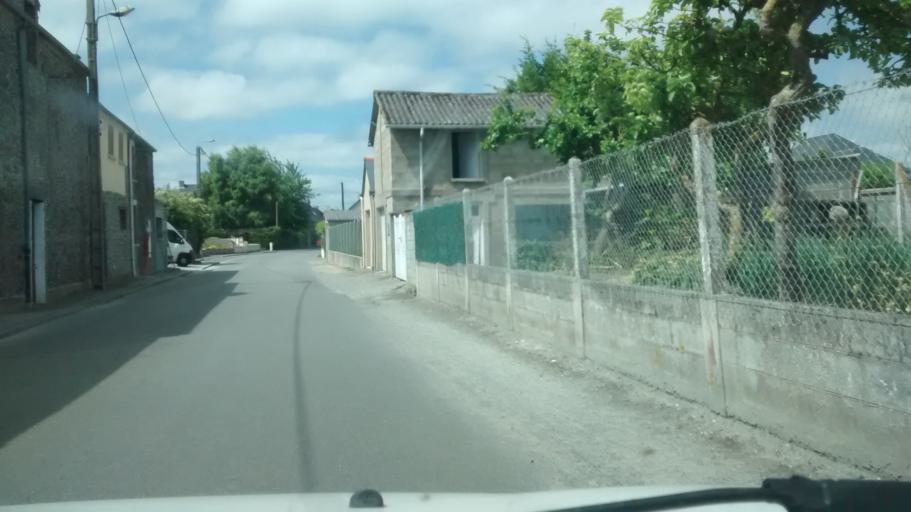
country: FR
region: Brittany
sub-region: Departement d'Ille-et-Vilaine
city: La Fresnais
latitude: 48.6198
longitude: -1.8560
